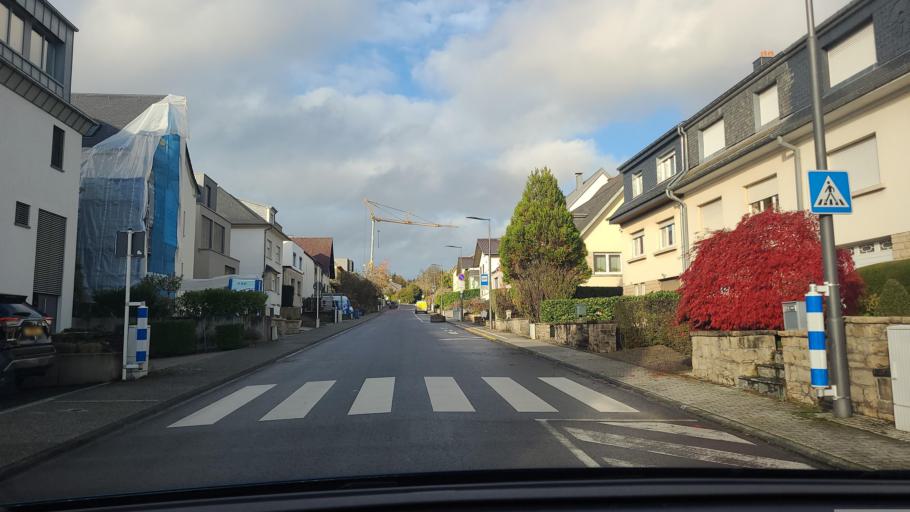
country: LU
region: Luxembourg
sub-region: Canton de Luxembourg
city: Strassen
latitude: 49.6229
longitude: 6.0698
